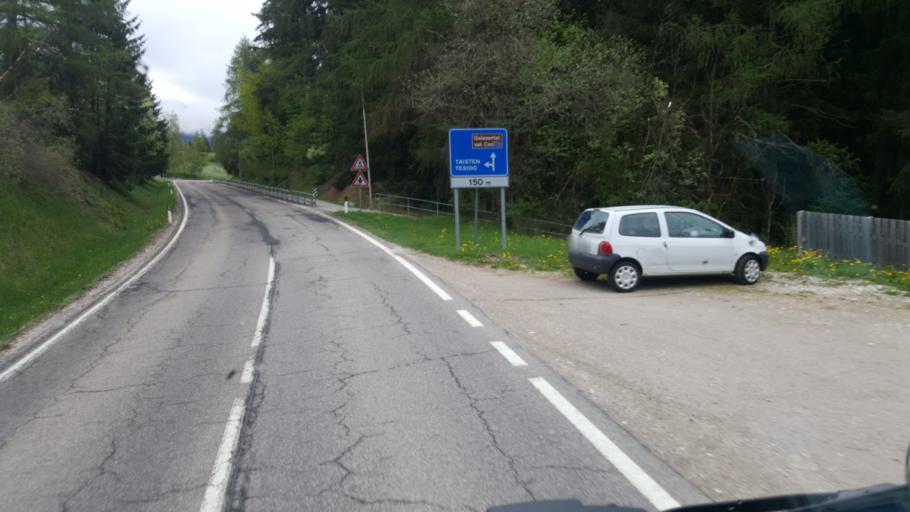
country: IT
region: Trentino-Alto Adige
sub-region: Bolzano
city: Monguelfo
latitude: 46.7598
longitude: 12.1069
